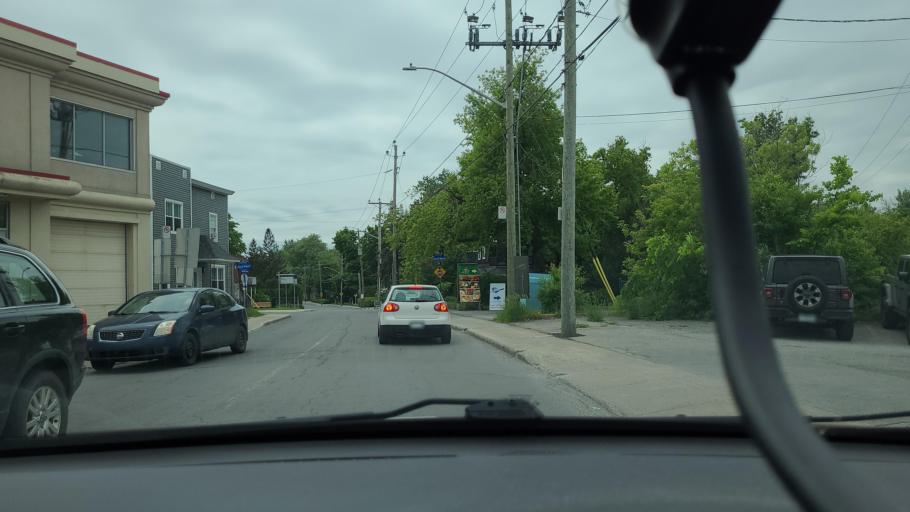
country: CA
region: Quebec
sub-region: Laurentides
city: Rosemere
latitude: 45.6109
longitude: -73.7925
